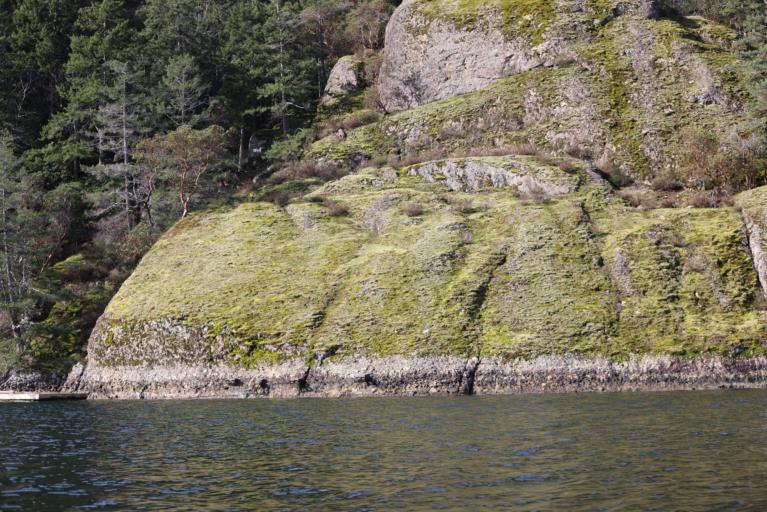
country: CA
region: British Columbia
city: North Cowichan
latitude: 48.7918
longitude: -123.5636
